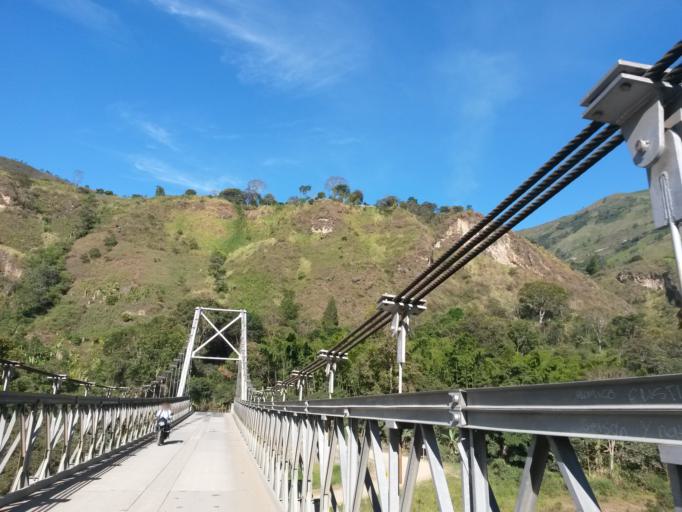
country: CO
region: Cauca
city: Belalcazar
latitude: 2.5791
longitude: -75.9797
